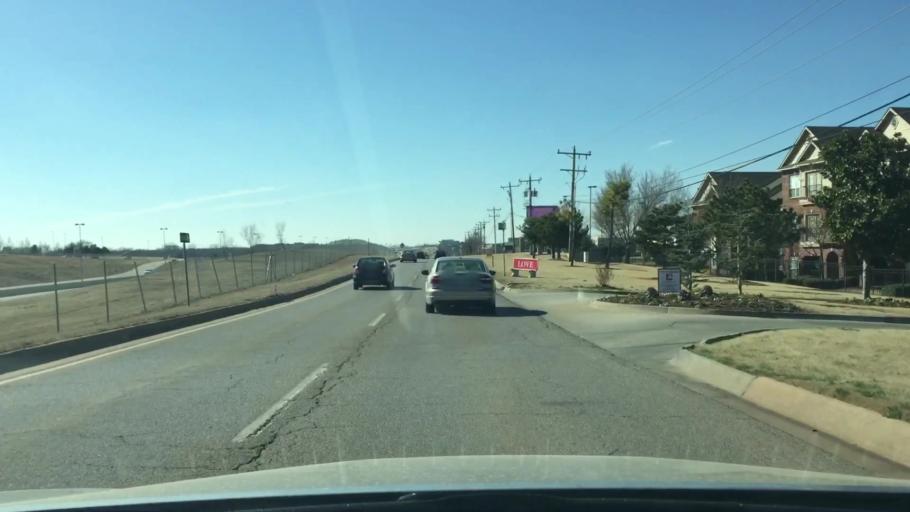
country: US
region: Oklahoma
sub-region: Oklahoma County
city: The Village
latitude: 35.6103
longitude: -97.5950
